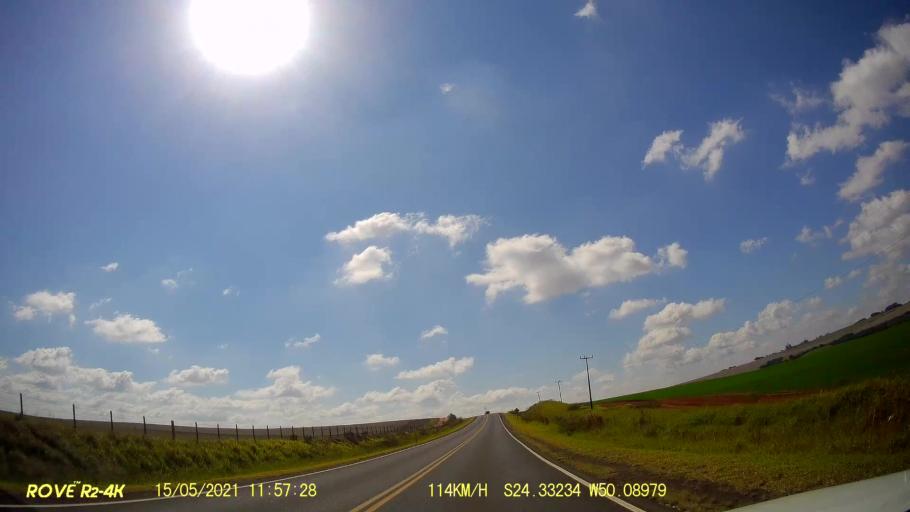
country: BR
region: Parana
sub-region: Pirai Do Sul
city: Pirai do Sul
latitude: -24.3351
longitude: -50.0902
